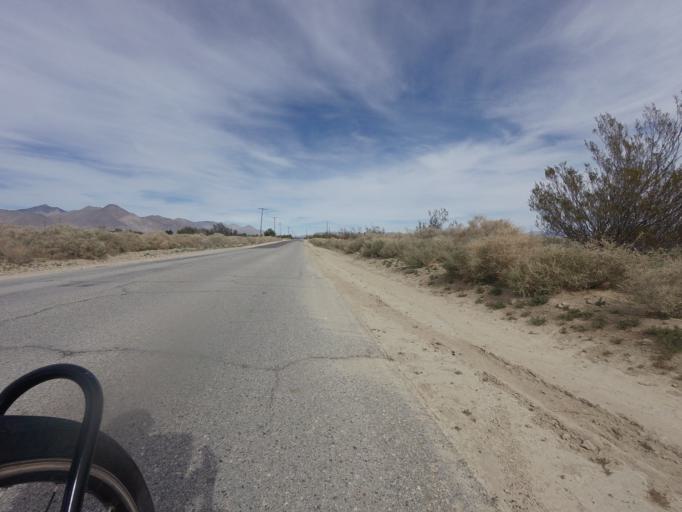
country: US
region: California
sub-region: Kern County
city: Inyokern
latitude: 35.7236
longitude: -117.8351
